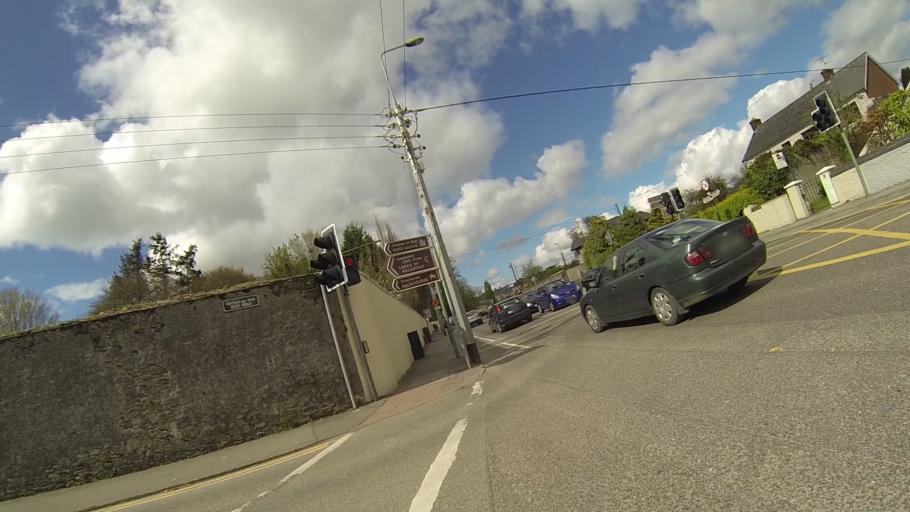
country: IE
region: Munster
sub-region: Ciarrai
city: Cill Airne
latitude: 52.0559
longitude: -9.5072
